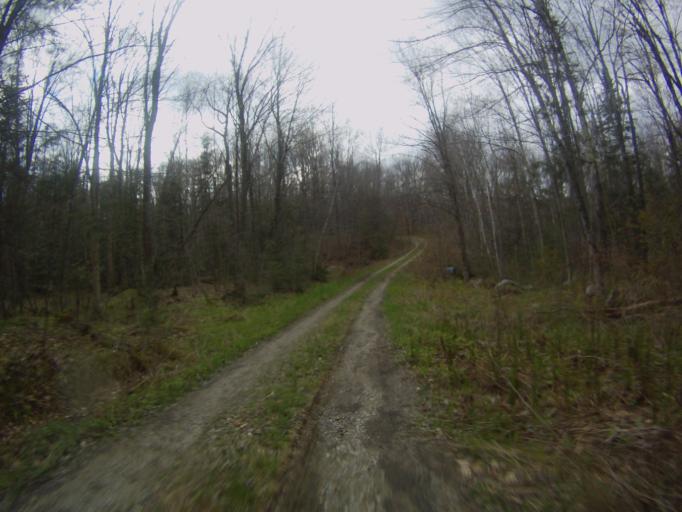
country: US
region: Vermont
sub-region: Addison County
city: Bristol
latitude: 44.0493
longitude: -73.0537
